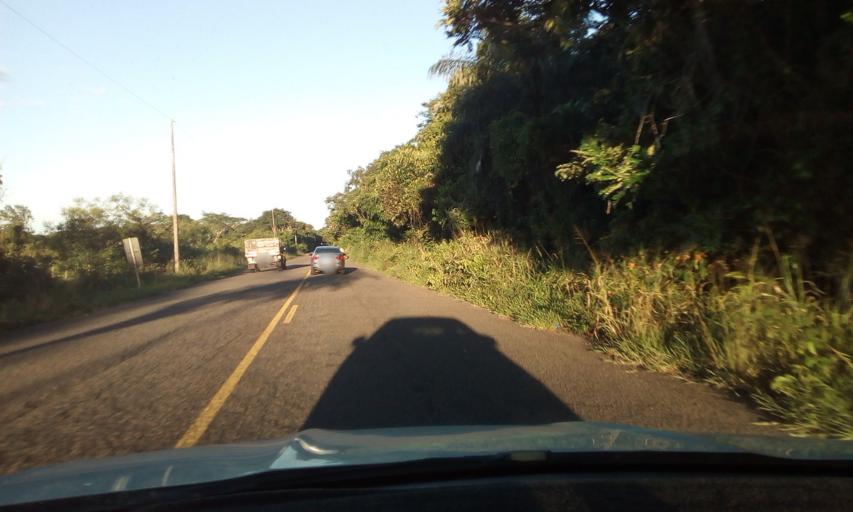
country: BR
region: Paraiba
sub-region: Areia
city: Remigio
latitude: -6.9642
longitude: -35.7478
